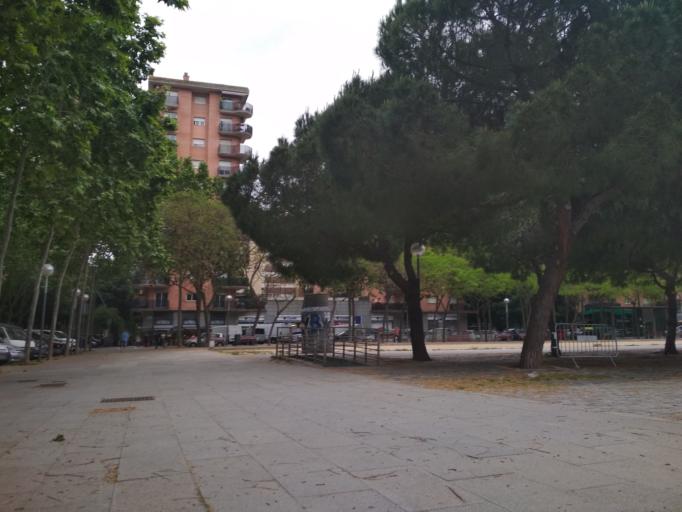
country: ES
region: Catalonia
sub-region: Provincia de Barcelona
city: Sant Marti
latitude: 41.4193
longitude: 2.2054
